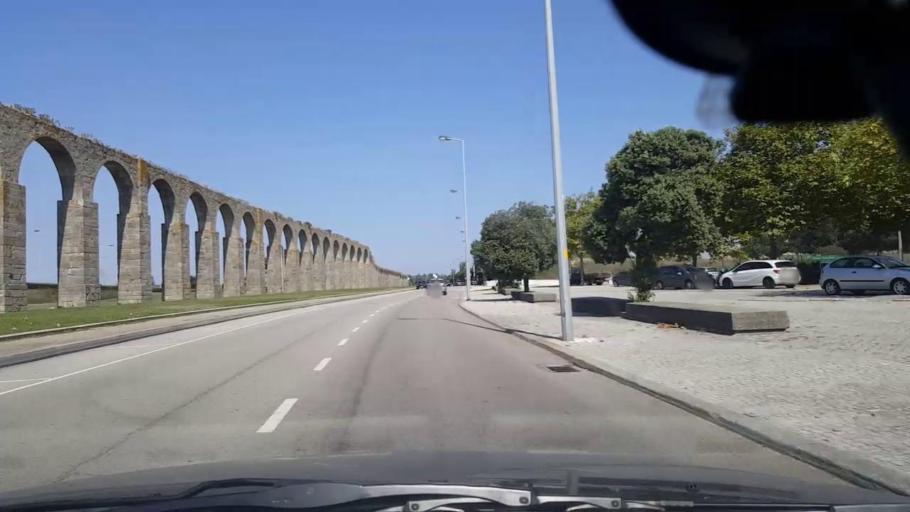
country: PT
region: Porto
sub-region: Vila do Conde
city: Vila do Conde
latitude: 41.3631
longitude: -8.7418
